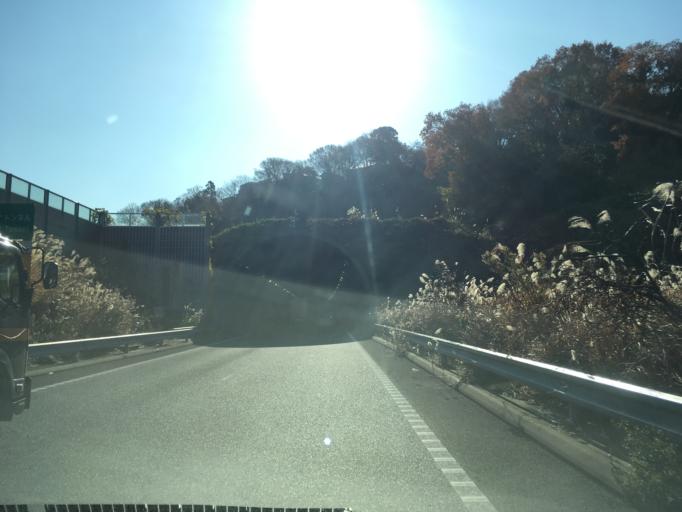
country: JP
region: Kanagawa
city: Zama
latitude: 35.5148
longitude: 139.3606
